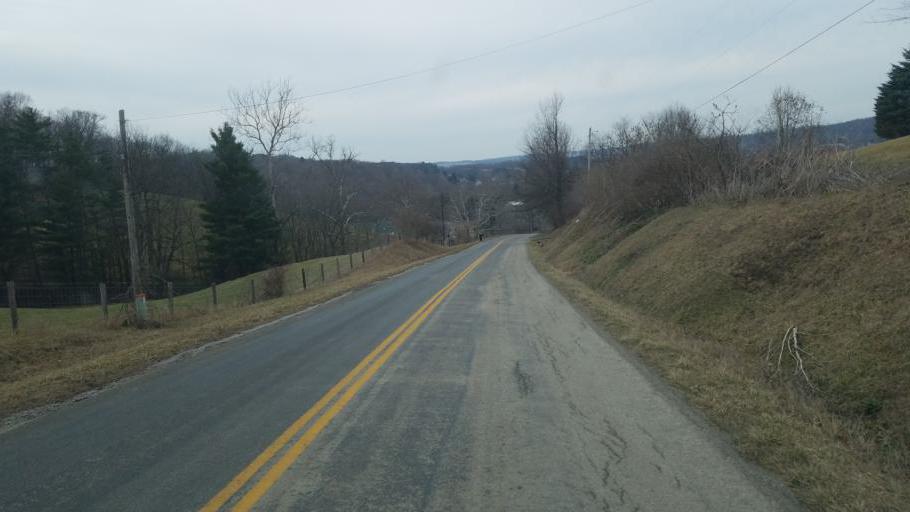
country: US
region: Ohio
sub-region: Ashland County
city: Loudonville
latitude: 40.6256
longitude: -82.2295
